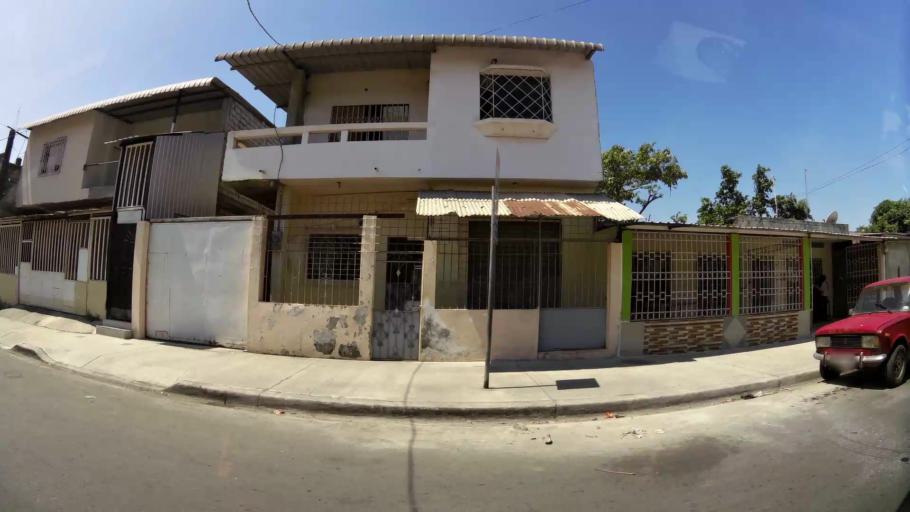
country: EC
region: Guayas
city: Guayaquil
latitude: -2.2330
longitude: -79.9193
